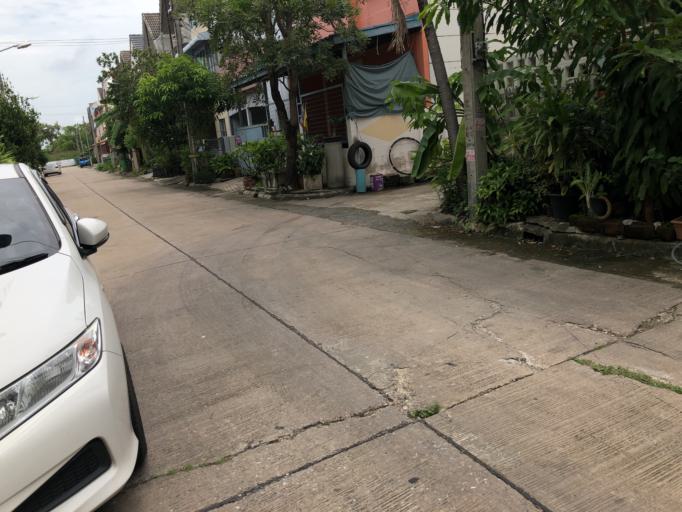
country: TH
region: Nonthaburi
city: Pak Kret
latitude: 13.9243
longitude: 100.5313
